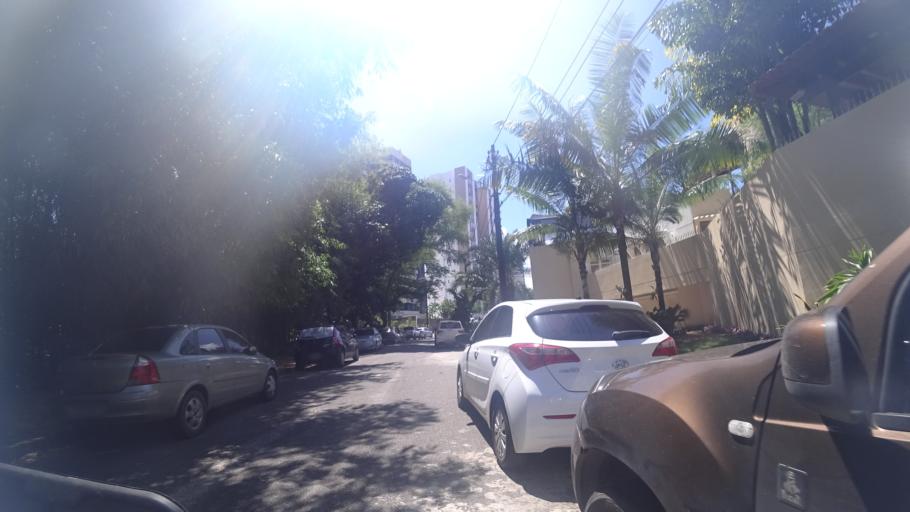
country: BR
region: Bahia
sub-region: Salvador
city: Salvador
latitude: -12.9918
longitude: -38.4661
